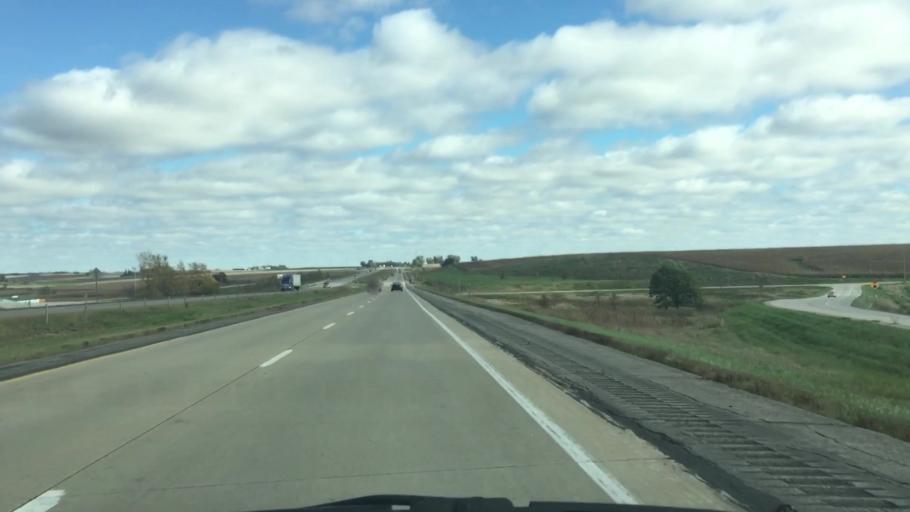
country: US
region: Iowa
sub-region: Poweshiek County
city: Brooklyn
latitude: 41.6959
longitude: -92.2838
